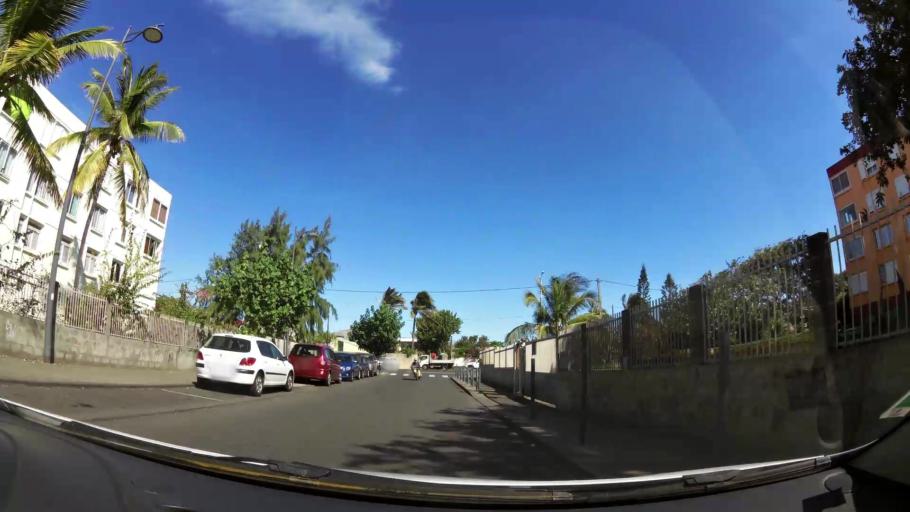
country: RE
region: Reunion
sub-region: Reunion
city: Saint-Pierre
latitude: -21.3409
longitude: 55.4629
